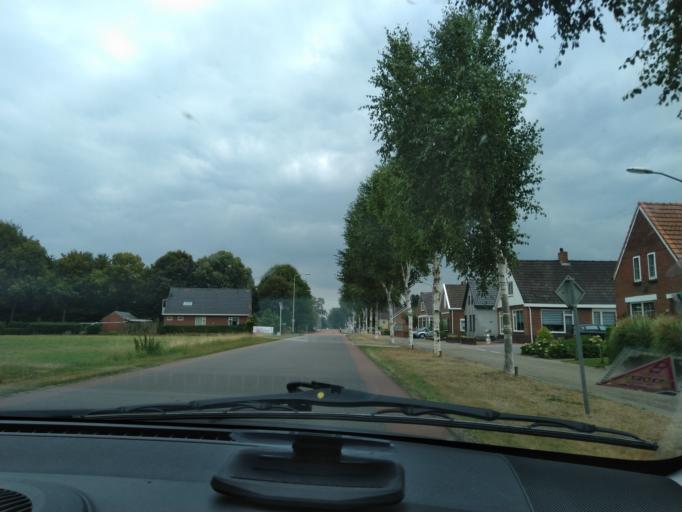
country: NL
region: Groningen
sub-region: Gemeente Vlagtwedde
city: Vlagtwedde
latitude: 53.0901
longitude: 7.1662
